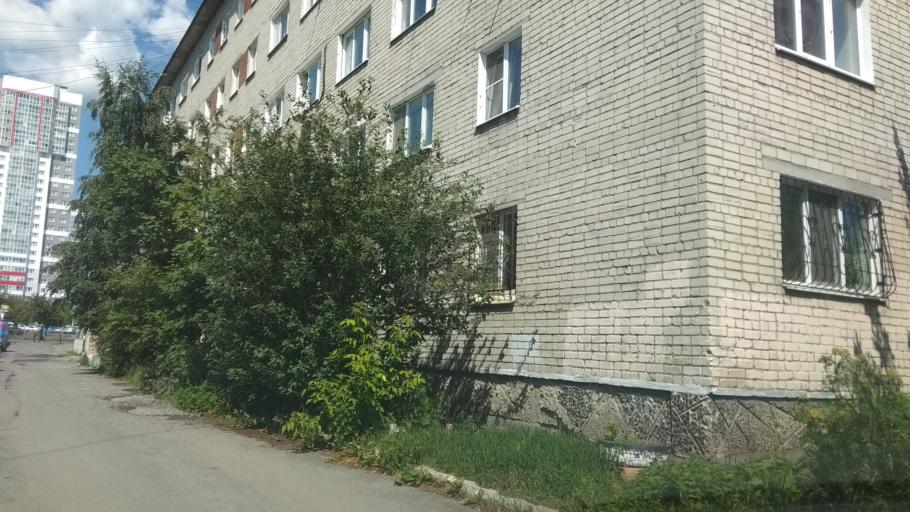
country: RU
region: Sverdlovsk
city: Yekaterinburg
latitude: 56.8340
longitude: 60.6909
